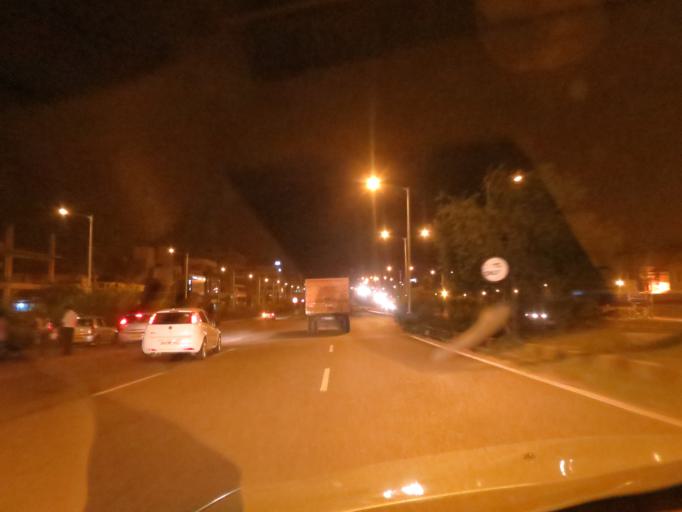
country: IN
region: Karnataka
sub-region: Bangalore Urban
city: Bangalore
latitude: 13.0227
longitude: 77.6469
